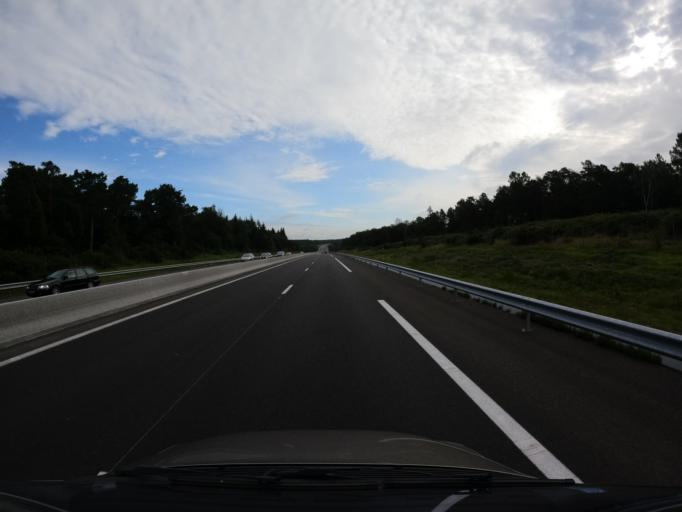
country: FR
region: Centre
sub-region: Departement d'Indre-et-Loire
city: Langeais
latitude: 47.3295
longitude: 0.3447
